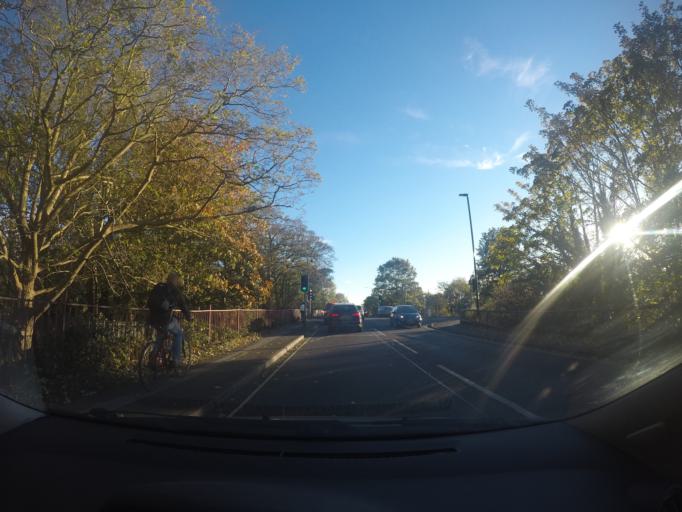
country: GB
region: England
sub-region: City of York
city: York
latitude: 53.9740
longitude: -1.0819
